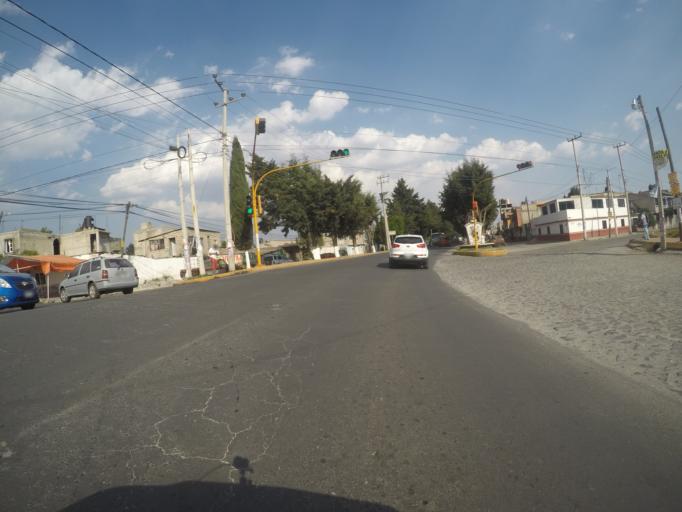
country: MX
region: Morelos
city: Chapultepec
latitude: 19.2033
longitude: -99.5513
